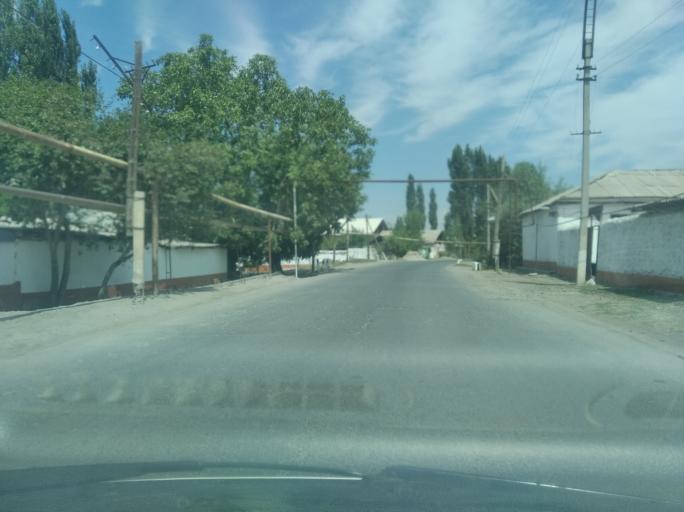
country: UZ
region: Andijon
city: Khujaobod
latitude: 40.6253
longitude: 72.4498
